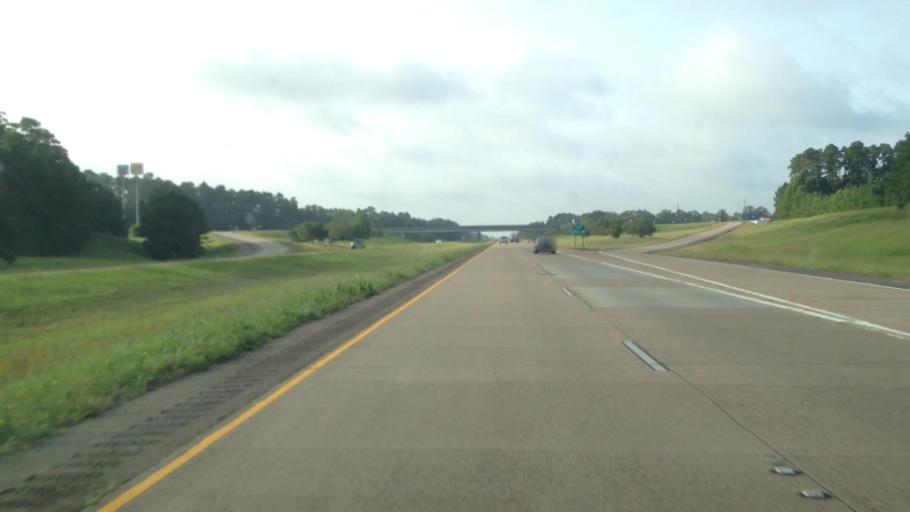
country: US
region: Louisiana
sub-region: Rapides Parish
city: Lecompte
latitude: 31.0756
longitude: -92.4359
